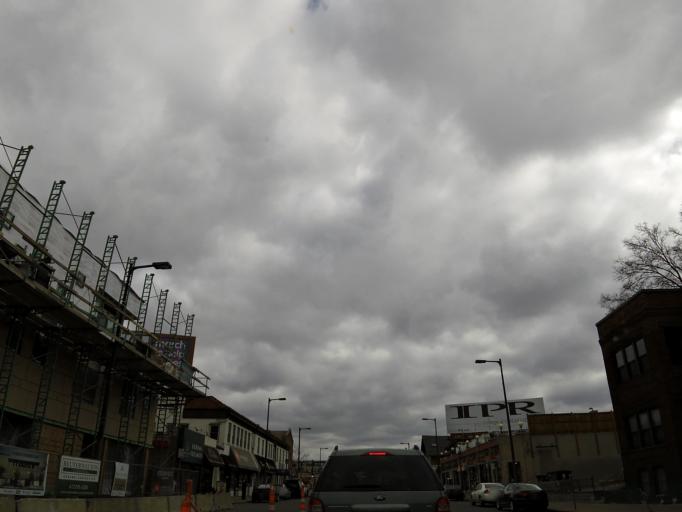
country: US
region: Minnesota
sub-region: Hennepin County
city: Saint Louis Park
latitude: 44.9484
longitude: -93.3033
